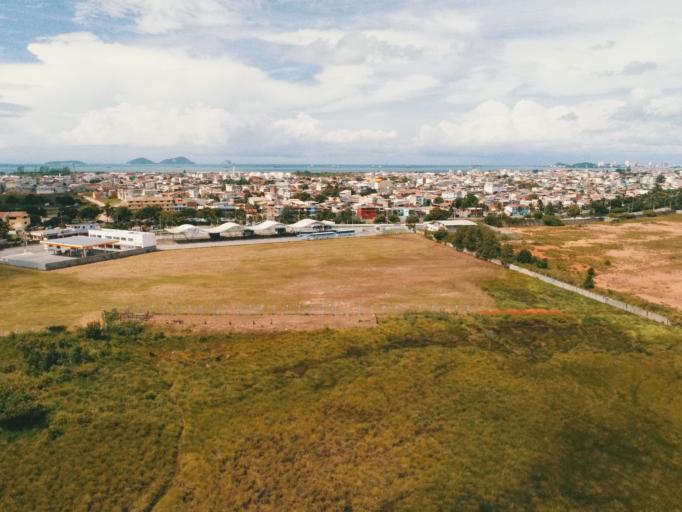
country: BR
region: Rio de Janeiro
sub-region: Macae
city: Macae
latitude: -22.3288
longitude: -41.7544
